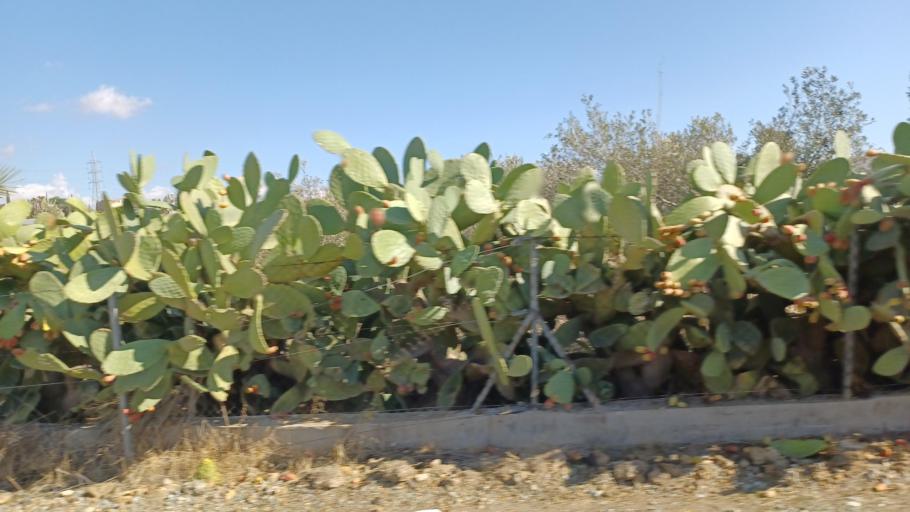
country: CY
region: Larnaka
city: Voroklini
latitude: 35.0020
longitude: 33.6530
